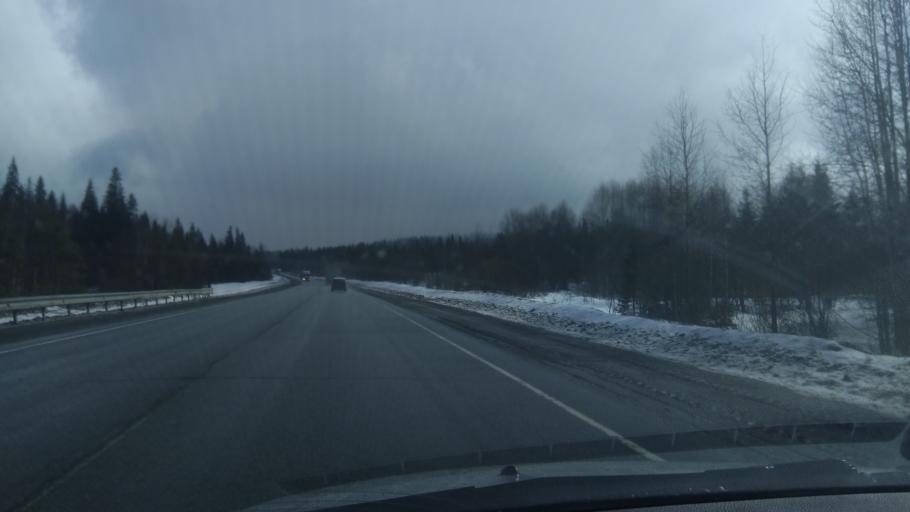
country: RU
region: Sverdlovsk
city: Arti
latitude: 56.7905
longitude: 58.4998
